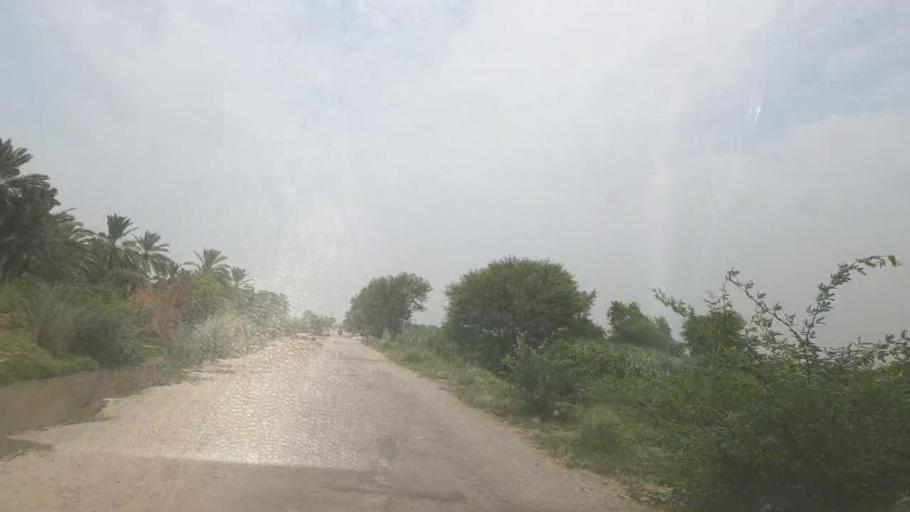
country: PK
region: Sindh
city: Kot Diji
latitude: 27.4270
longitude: 68.6502
